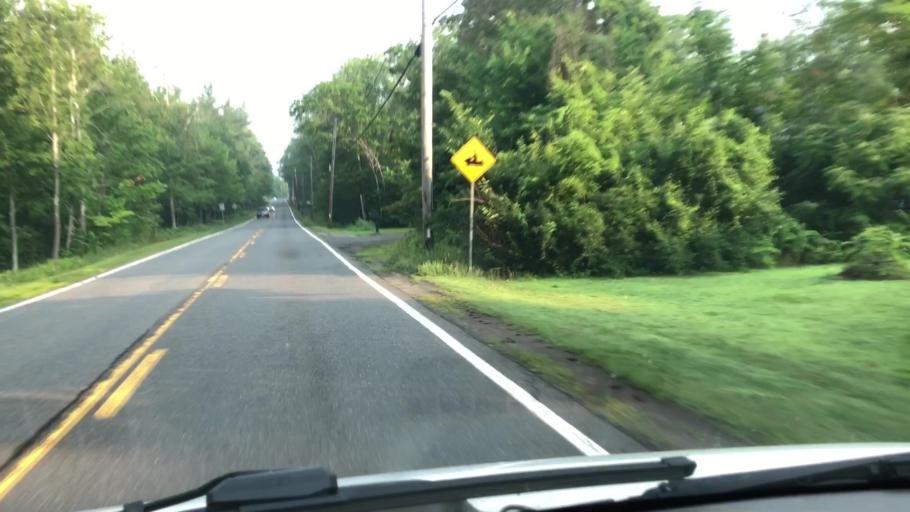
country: US
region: Massachusetts
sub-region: Hampshire County
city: Chesterfield
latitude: 42.4328
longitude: -72.7921
